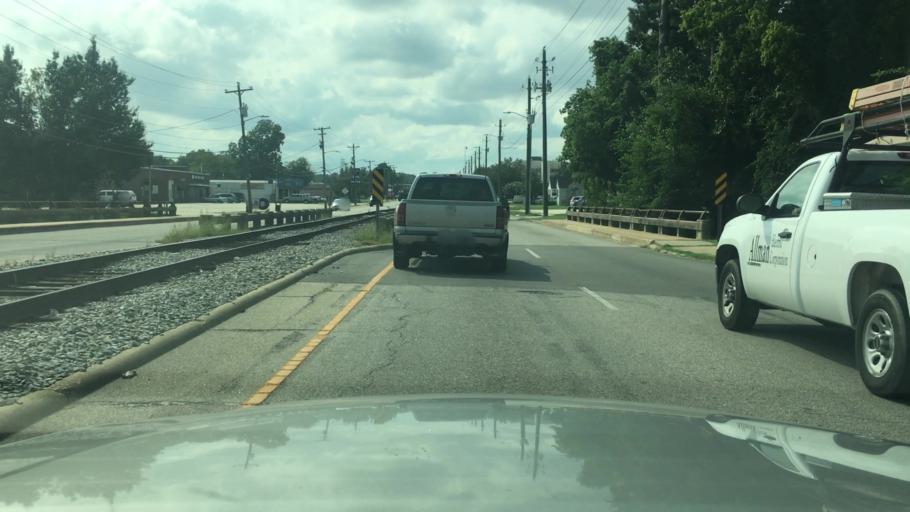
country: US
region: North Carolina
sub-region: Cumberland County
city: Fayetteville
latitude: 35.0479
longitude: -78.8713
